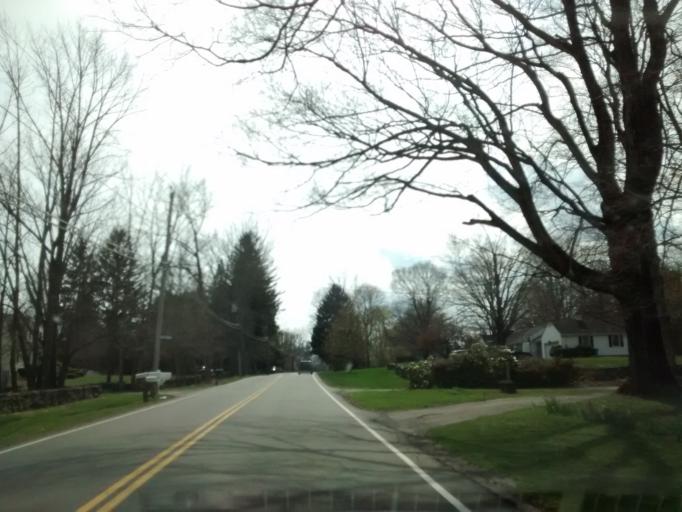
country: US
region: Massachusetts
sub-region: Worcester County
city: Sutton
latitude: 42.1397
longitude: -71.7810
